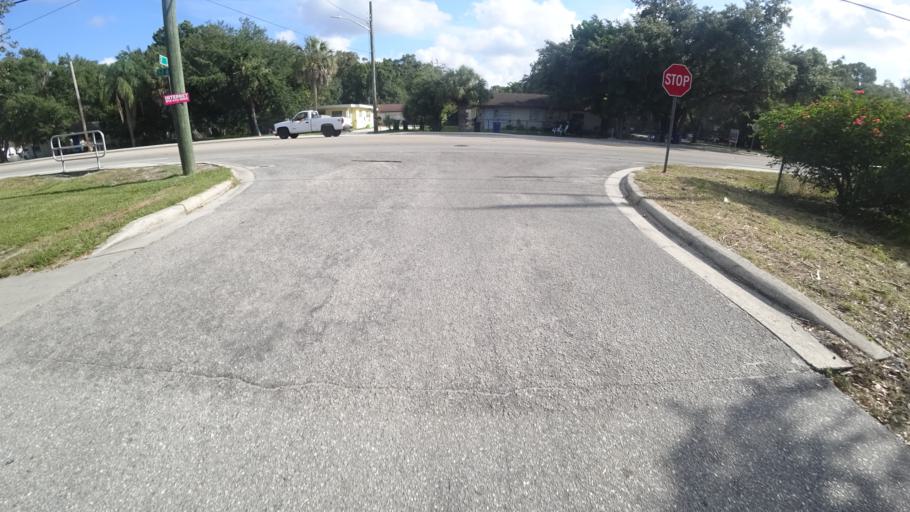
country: US
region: Florida
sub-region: Manatee County
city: West Samoset
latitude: 27.4401
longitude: -82.5570
